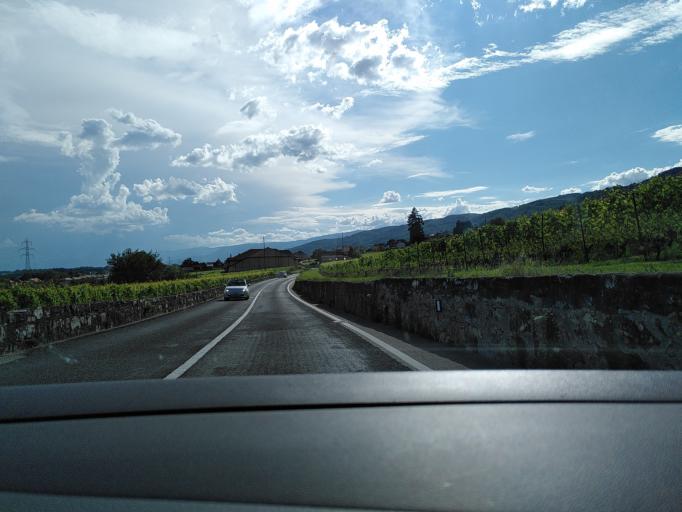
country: CH
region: Vaud
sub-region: Nyon District
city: Perroy
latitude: 46.4714
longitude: 6.3483
